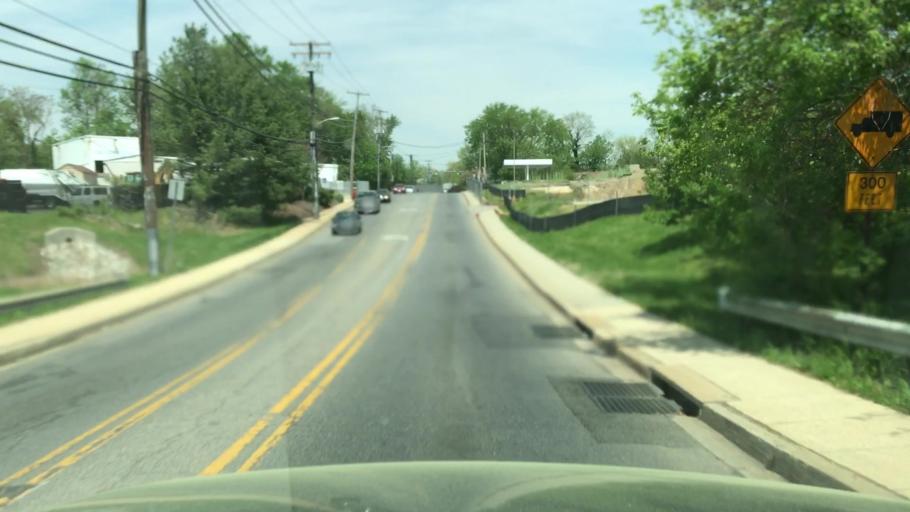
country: US
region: Maryland
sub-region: Anne Arundel County
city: Robinwood
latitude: 38.9716
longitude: -76.5102
